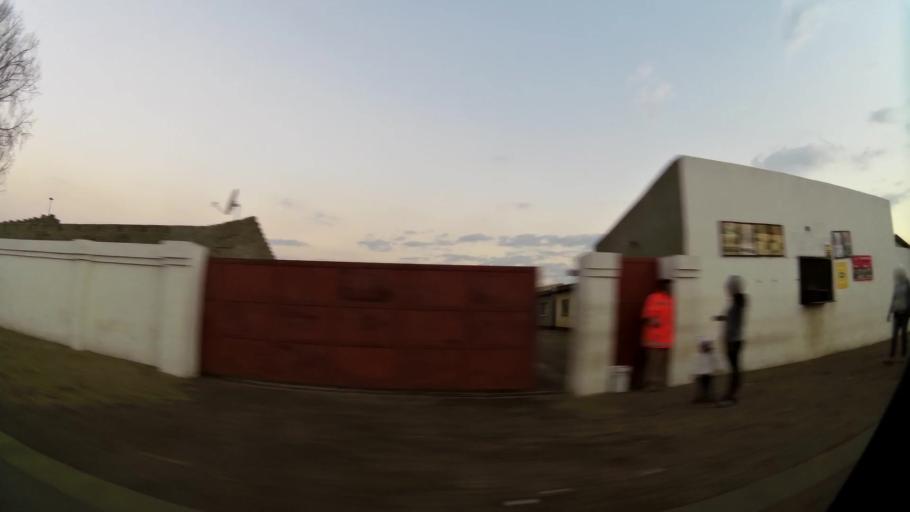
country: ZA
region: Gauteng
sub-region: City of Johannesburg Metropolitan Municipality
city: Orange Farm
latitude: -26.5471
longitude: 27.8364
